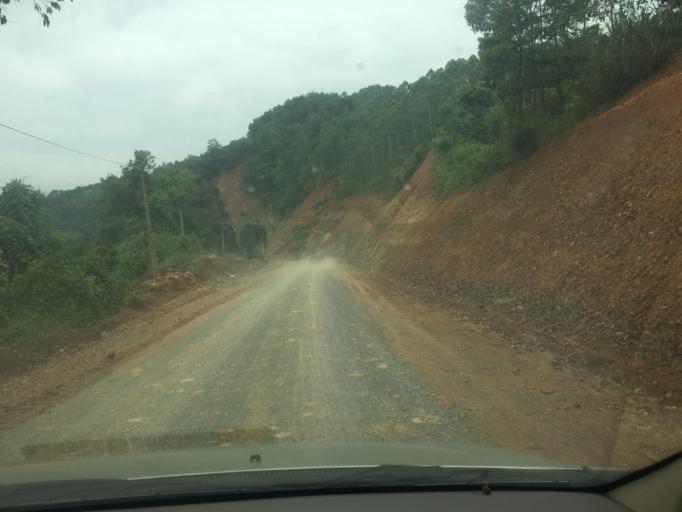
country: VN
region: Lang Son
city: Binh Gia
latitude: 22.1296
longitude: 106.3511
